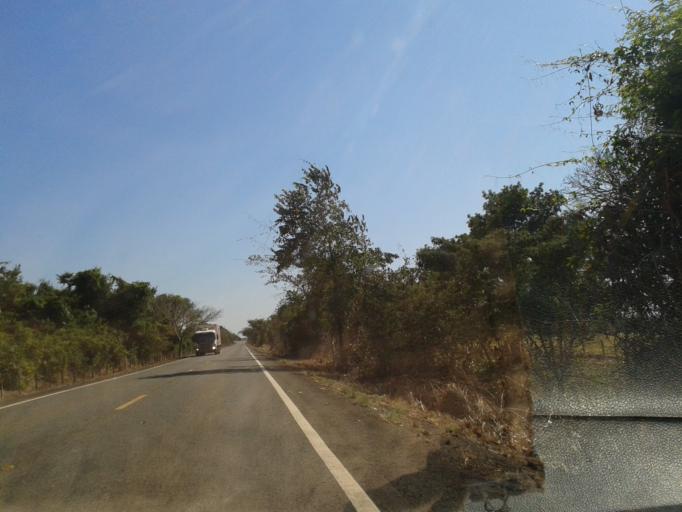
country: BR
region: Goias
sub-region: Sao Miguel Do Araguaia
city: Sao Miguel do Araguaia
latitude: -13.8986
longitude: -50.3270
